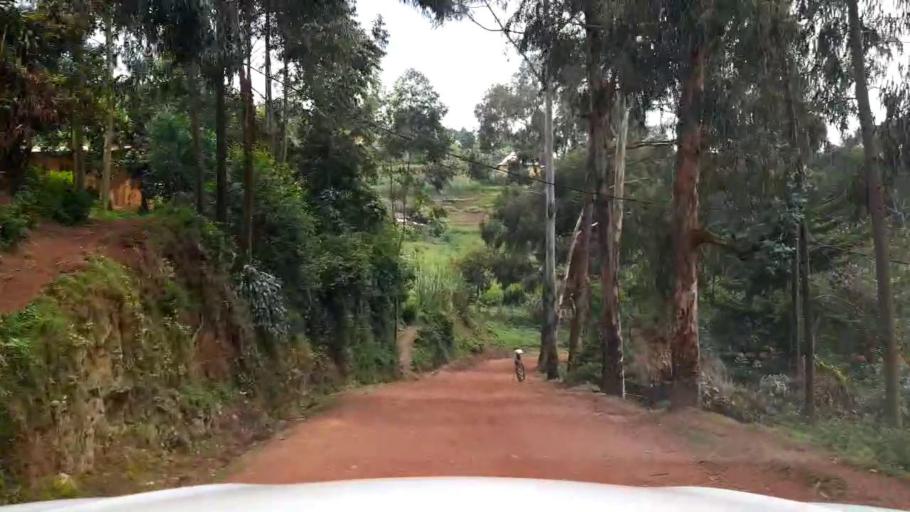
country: UG
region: Western Region
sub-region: Kisoro District
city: Kisoro
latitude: -1.4180
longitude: 29.8299
